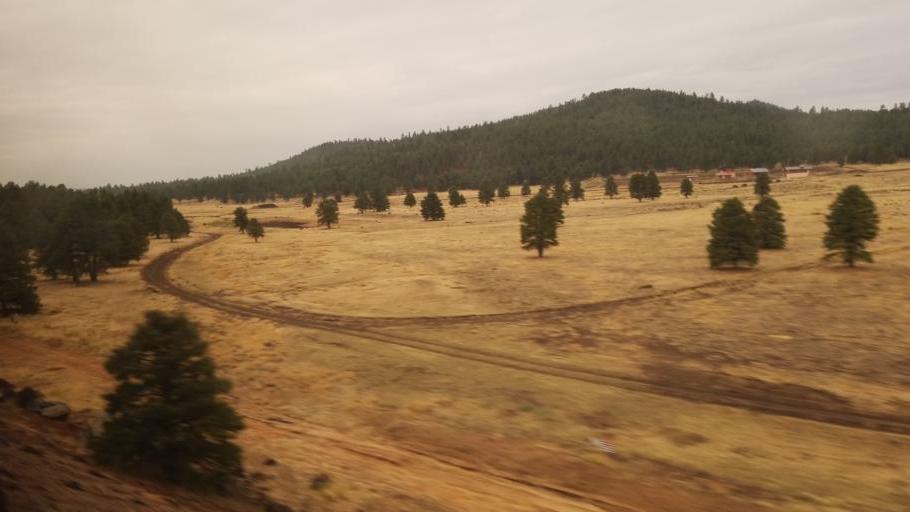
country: US
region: Arizona
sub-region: Coconino County
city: Parks
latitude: 35.2458
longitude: -111.8886
